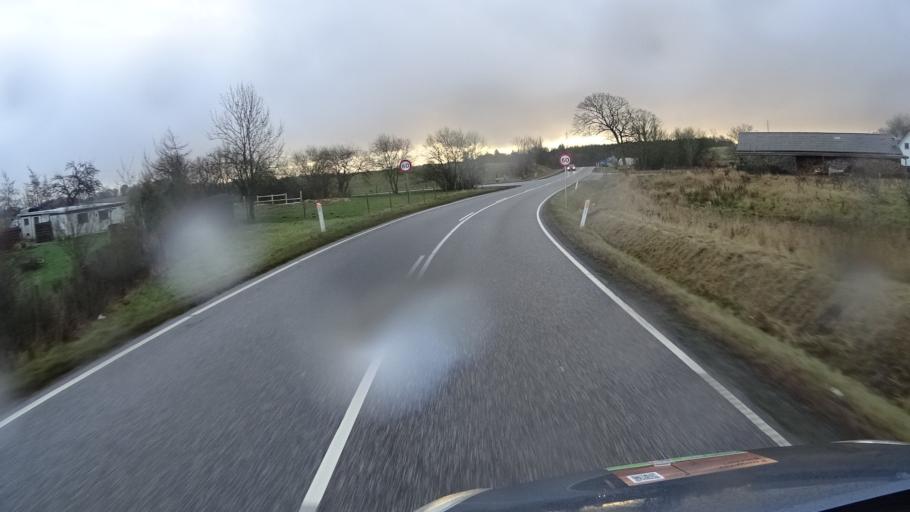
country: DK
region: South Denmark
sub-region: Vejle Kommune
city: Vejle
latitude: 55.7416
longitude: 9.5039
